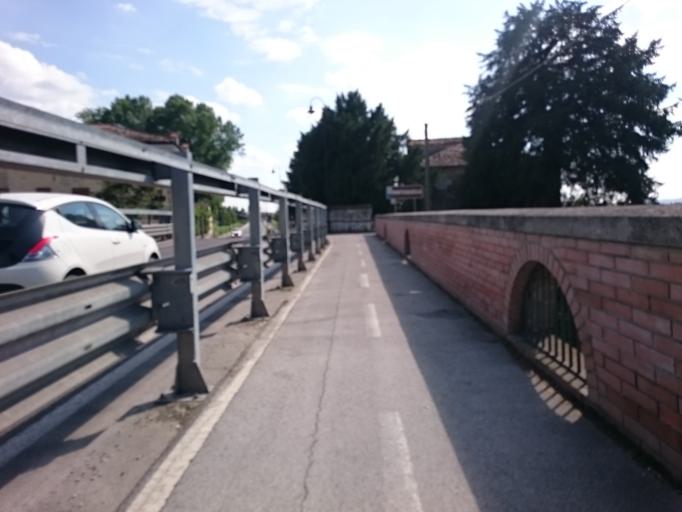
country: IT
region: Veneto
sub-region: Provincia di Vicenza
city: Montegalda
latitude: 45.4429
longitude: 11.6723
